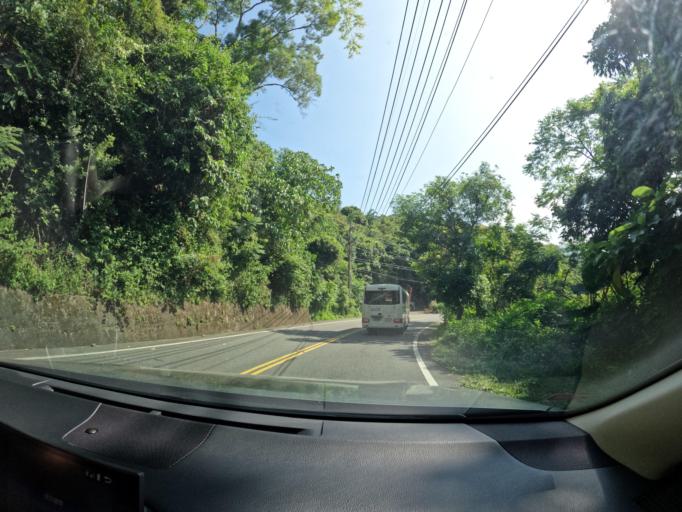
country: TW
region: Taiwan
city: Yujing
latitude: 23.0708
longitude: 120.6635
